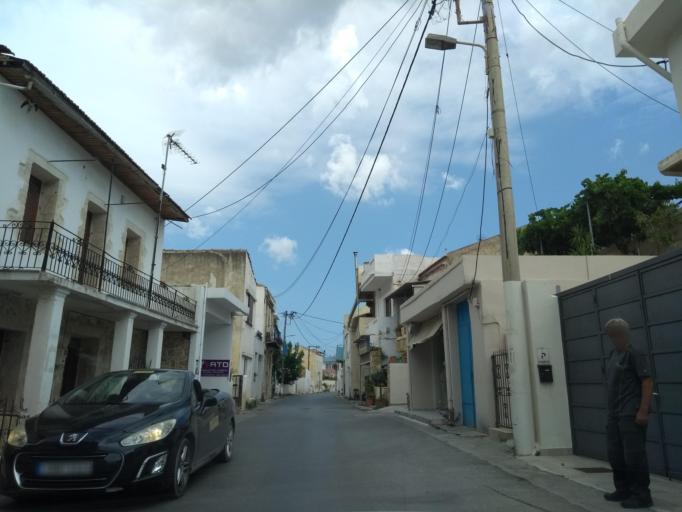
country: GR
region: Crete
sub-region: Nomos Chanias
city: Kalivai
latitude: 35.4544
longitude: 24.1710
